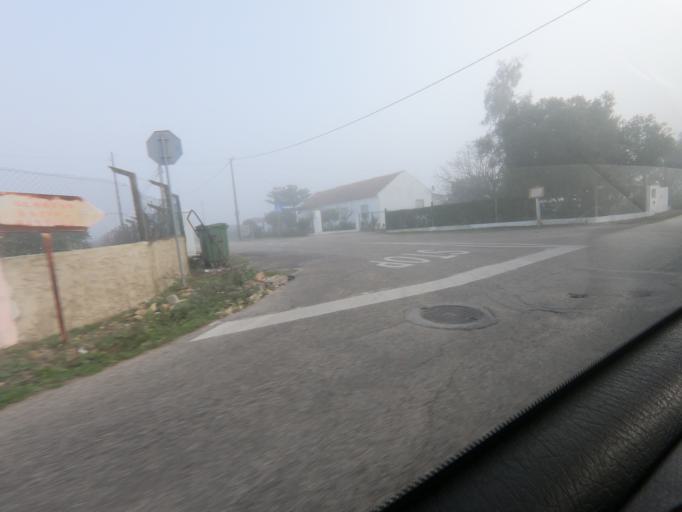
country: PT
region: Setubal
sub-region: Palmela
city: Pinhal Novo
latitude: 38.6109
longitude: -8.8719
